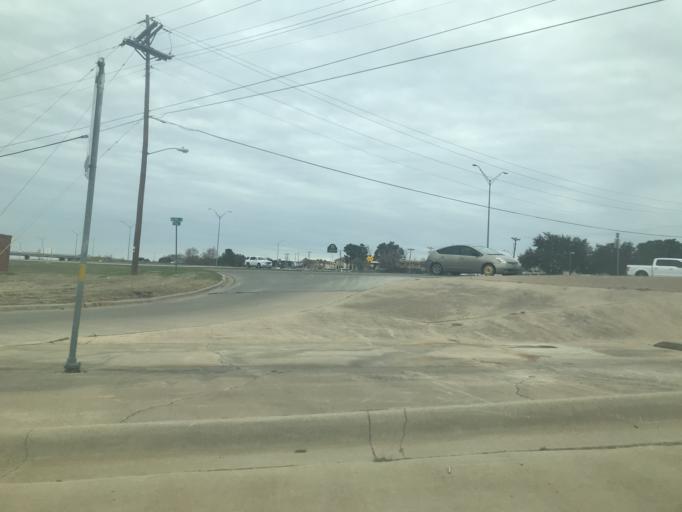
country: US
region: Texas
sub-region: Tom Green County
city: San Angelo
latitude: 31.4183
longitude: -100.4772
